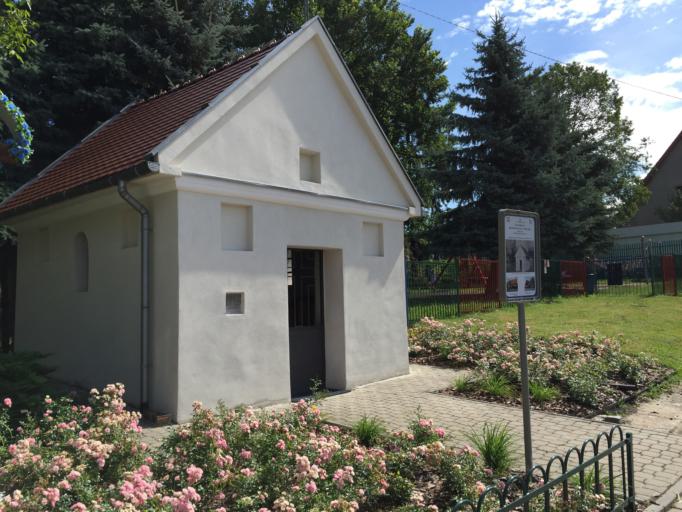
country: PL
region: Lesser Poland Voivodeship
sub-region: Powiat krakowski
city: Rzaska
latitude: 50.0865
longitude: 19.8799
